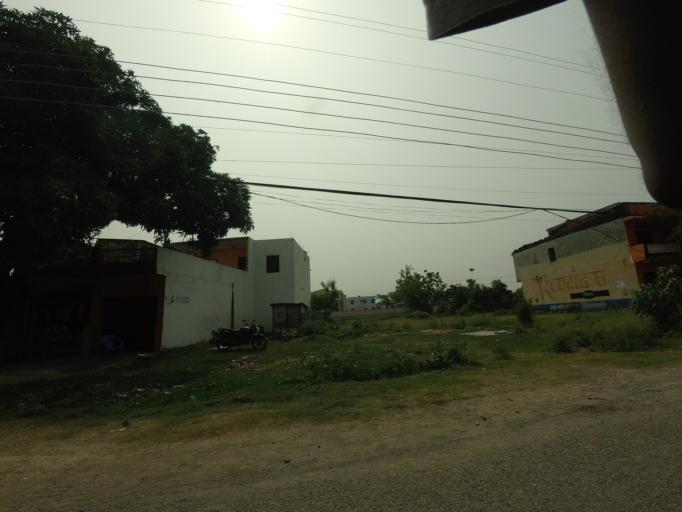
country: IN
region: Uttar Pradesh
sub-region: Maharajganj
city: Nautanwa
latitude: 27.4939
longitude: 83.2844
